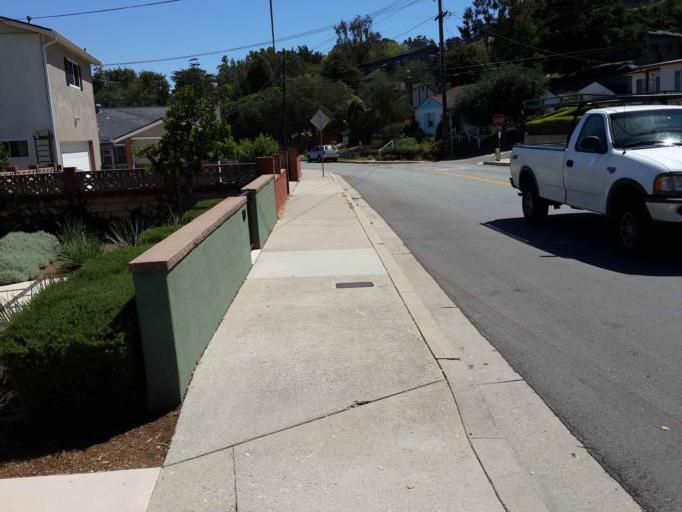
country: US
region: California
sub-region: San Luis Obispo County
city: San Luis Obispo
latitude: 35.2890
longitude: -120.6717
